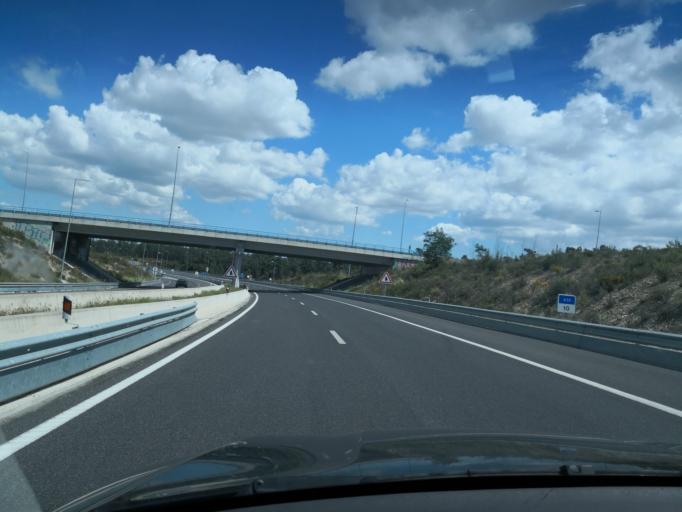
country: PT
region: Setubal
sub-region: Seixal
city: Amora
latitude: 38.6027
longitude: -9.1314
